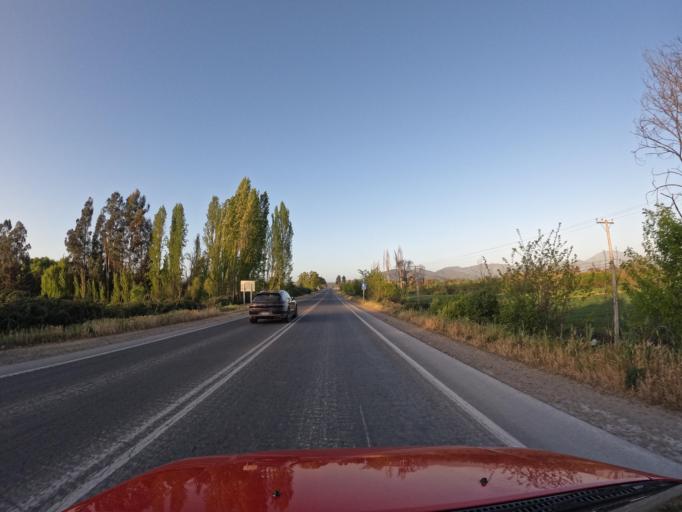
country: CL
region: O'Higgins
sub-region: Provincia de Cachapoal
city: San Vicente
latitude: -34.1642
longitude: -71.3943
